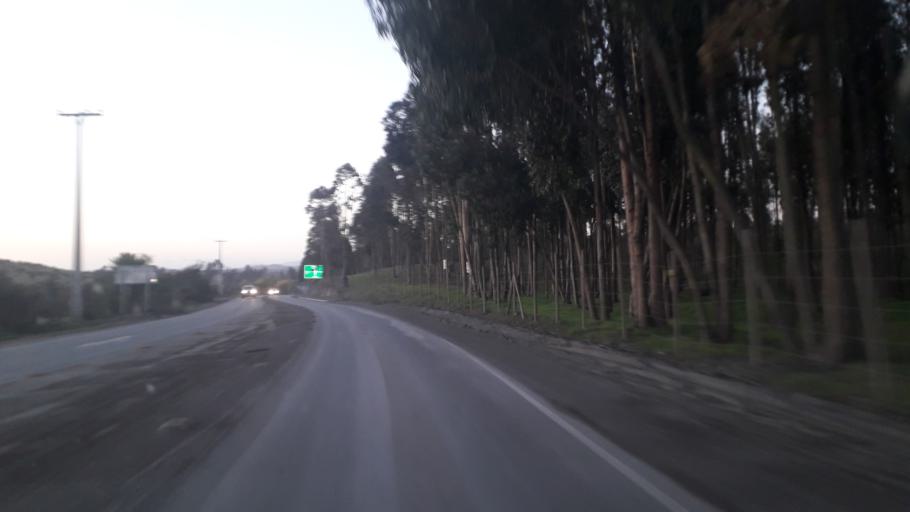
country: CL
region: Valparaiso
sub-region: Provincia de Quillota
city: Hacienda La Calera
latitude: -32.7454
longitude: -71.4180
